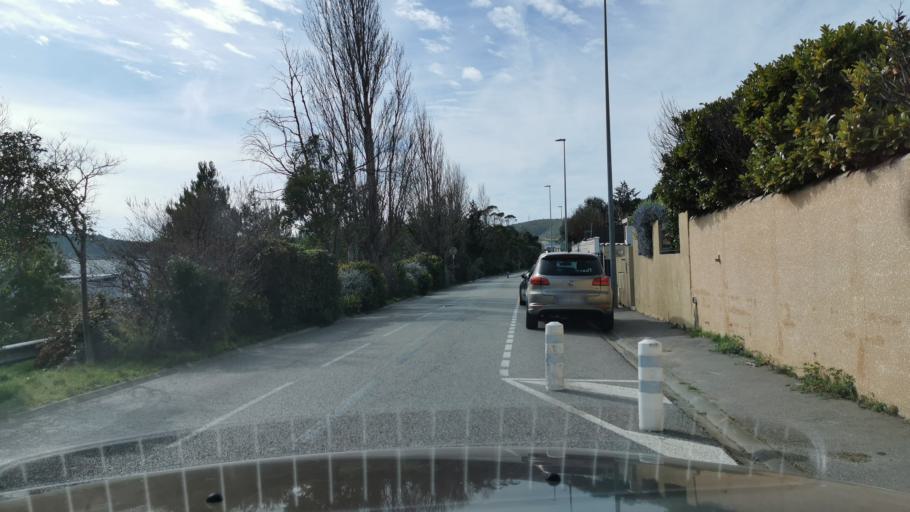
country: FR
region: Languedoc-Roussillon
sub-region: Departement de l'Aude
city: Narbonne
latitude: 43.1625
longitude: 2.9772
